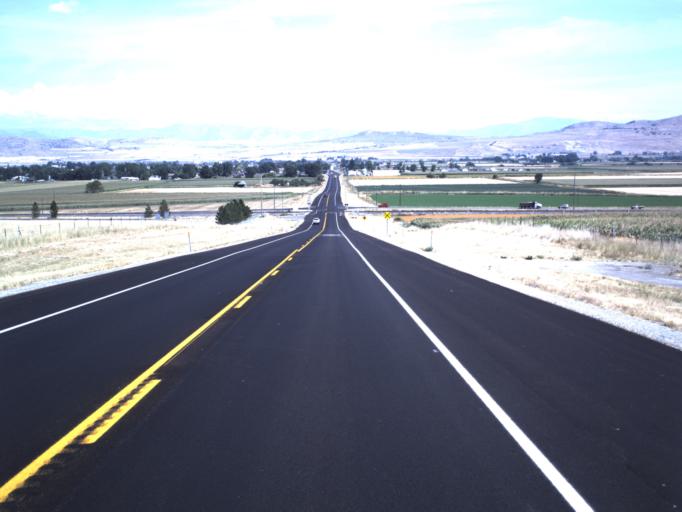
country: US
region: Utah
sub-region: Box Elder County
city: Garland
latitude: 41.7846
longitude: -112.1688
